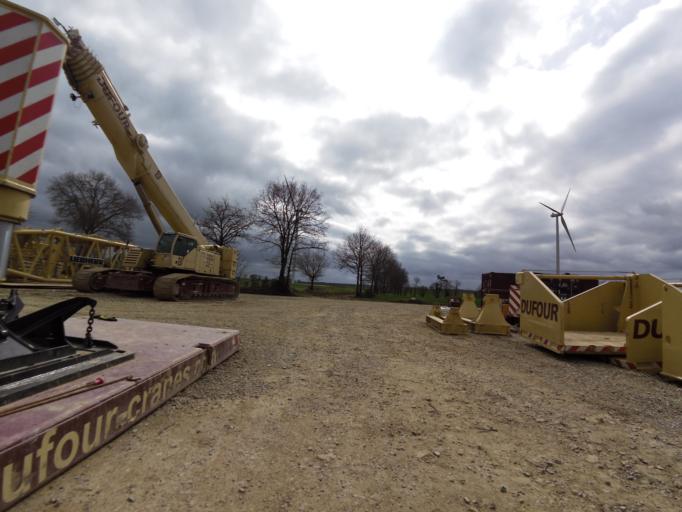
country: FR
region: Brittany
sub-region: Departement d'Ille-et-Vilaine
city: Chanteloup
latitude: 47.9369
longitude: -1.6270
